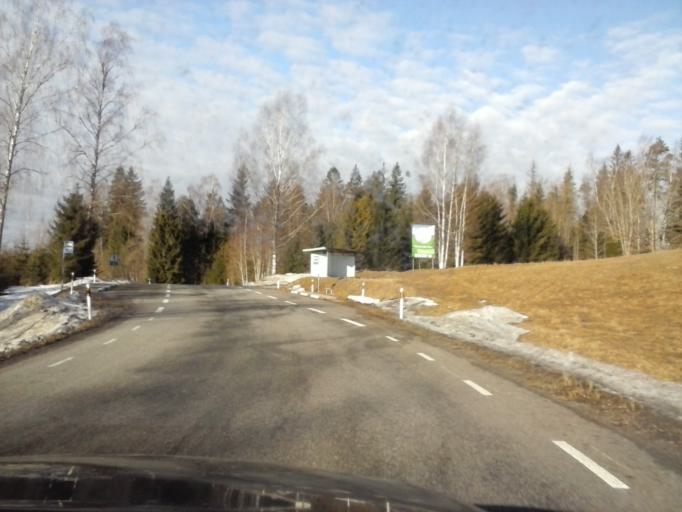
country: EE
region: Tartu
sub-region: Elva linn
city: Elva
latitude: 58.0473
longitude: 26.4066
